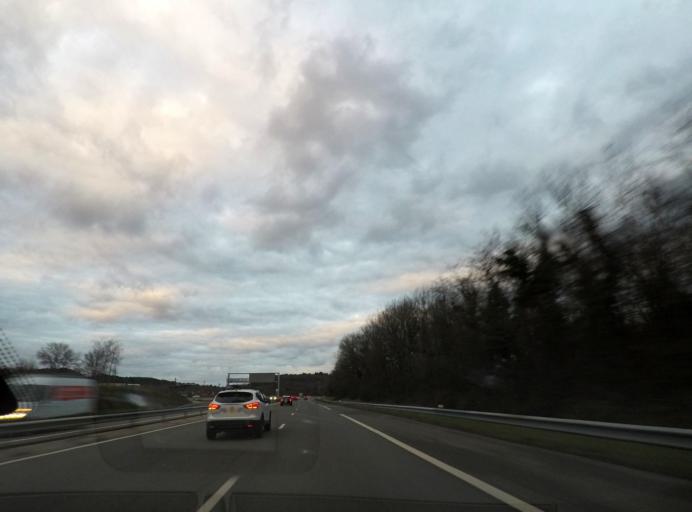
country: FR
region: Rhone-Alpes
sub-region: Departement de l'Ain
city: Saint-Martin-du-Frene
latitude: 46.1160
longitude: 5.4909
